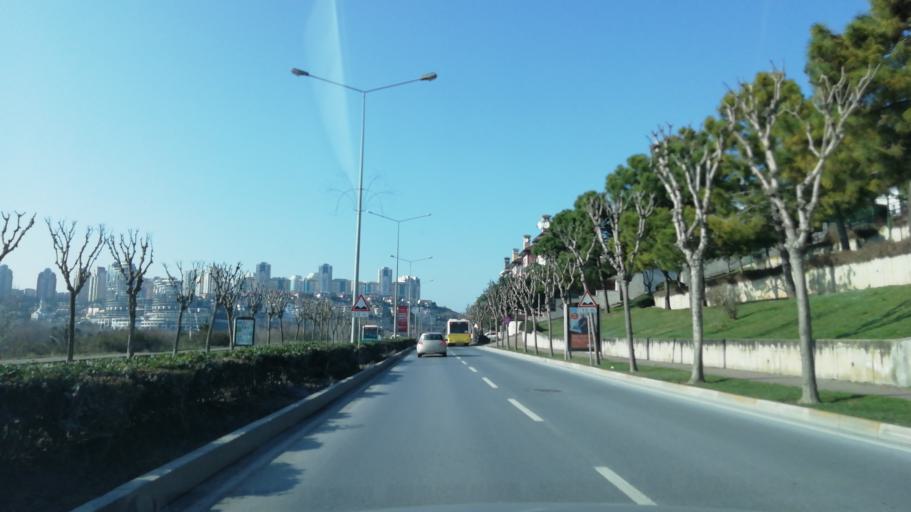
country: TR
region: Istanbul
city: Esenyurt
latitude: 41.0669
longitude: 28.6970
